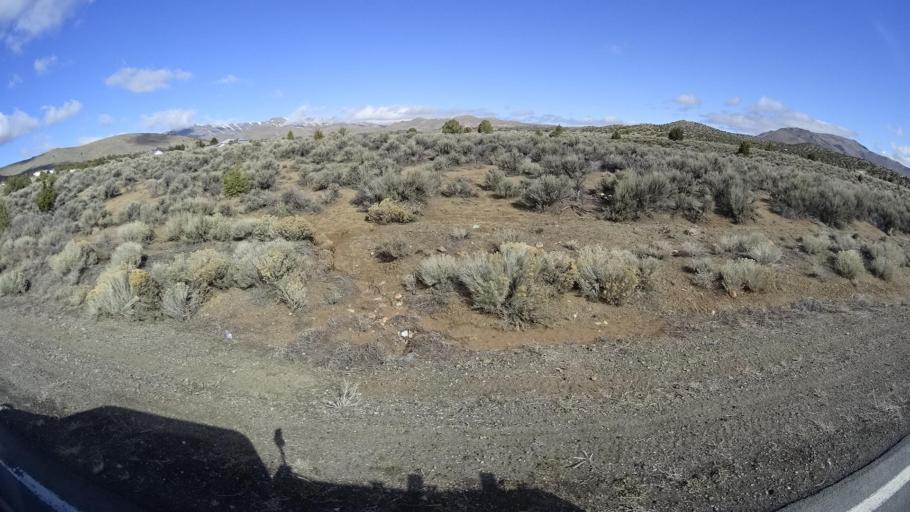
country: US
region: Nevada
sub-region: Washoe County
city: Cold Springs
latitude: 39.7162
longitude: -119.8938
